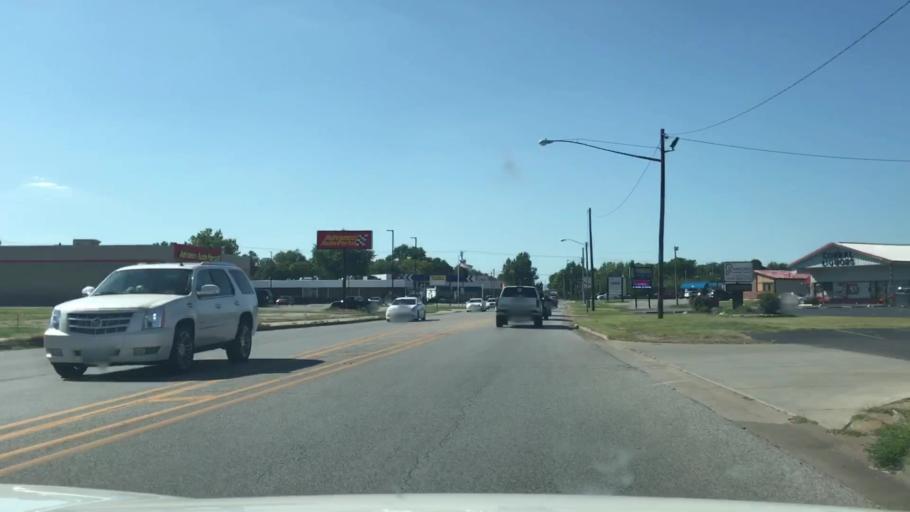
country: US
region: Illinois
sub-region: Madison County
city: Roxana
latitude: 38.8642
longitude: -90.0799
